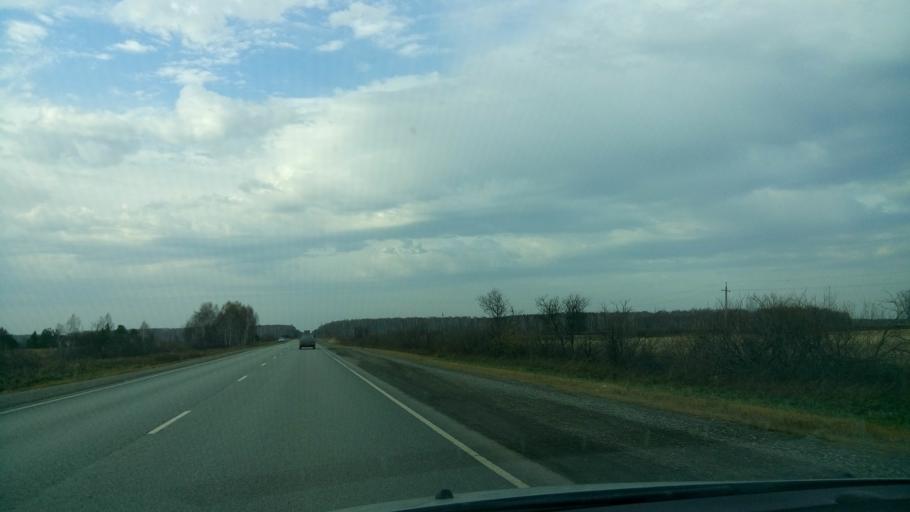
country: RU
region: Sverdlovsk
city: Baraba
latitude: 56.7755
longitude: 61.8344
